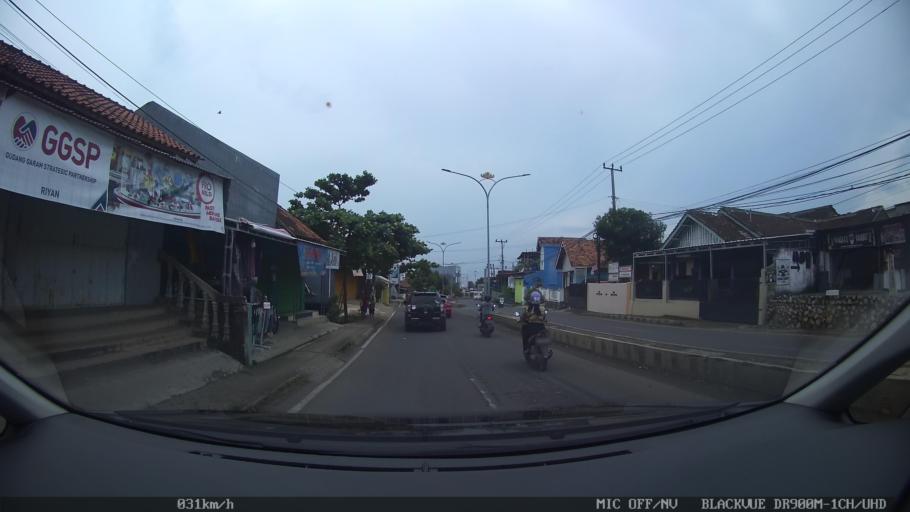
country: ID
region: Lampung
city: Kedaton
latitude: -5.3883
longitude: 105.2201
